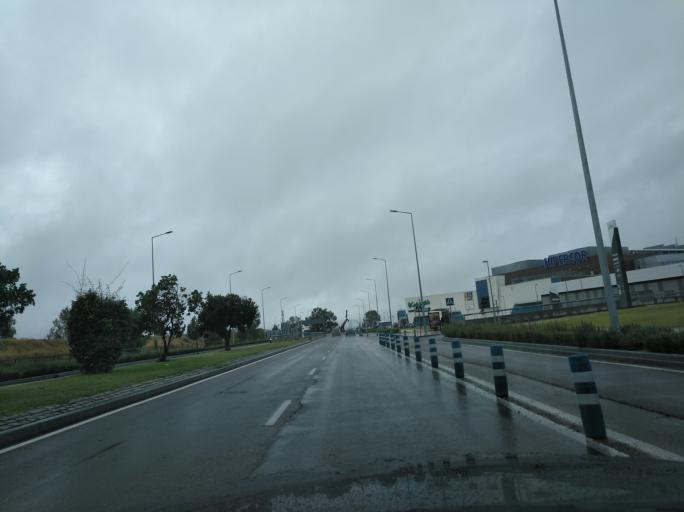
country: ES
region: Extremadura
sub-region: Provincia de Badajoz
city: Badajoz
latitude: 38.8828
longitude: -7.0217
